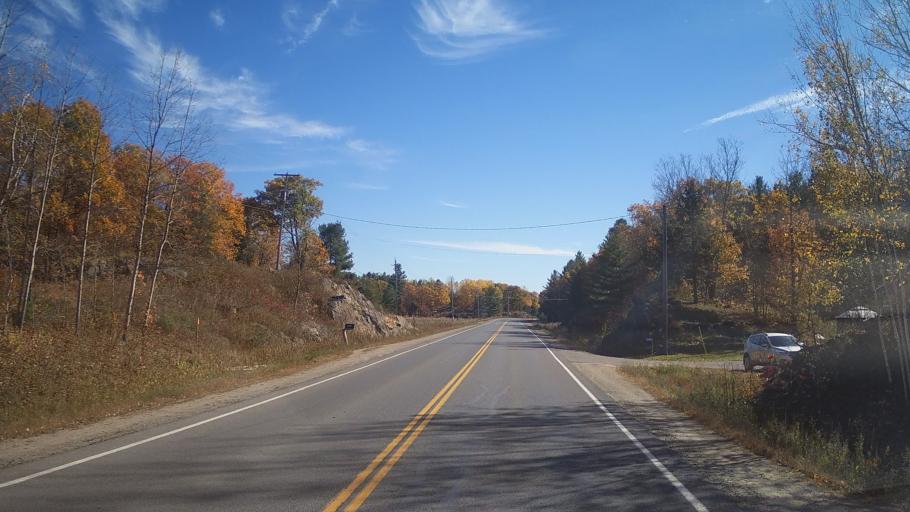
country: CA
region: Ontario
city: Perth
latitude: 44.7254
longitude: -76.6784
